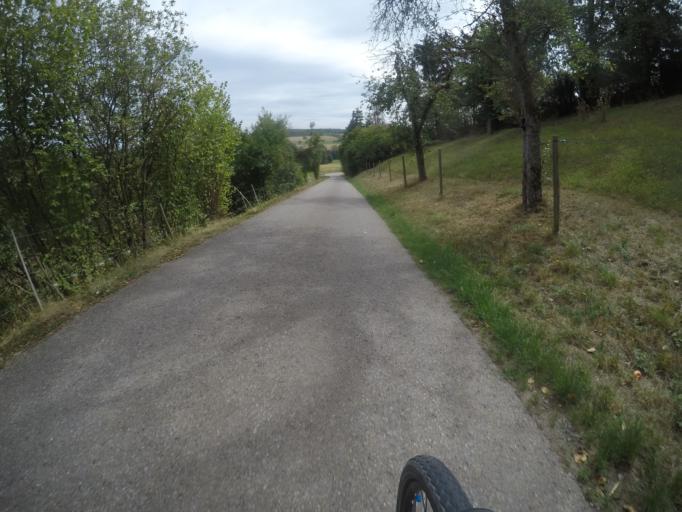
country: DE
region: Baden-Wuerttemberg
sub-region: Regierungsbezirk Stuttgart
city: Oberriexingen
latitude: 48.9288
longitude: 8.9971
